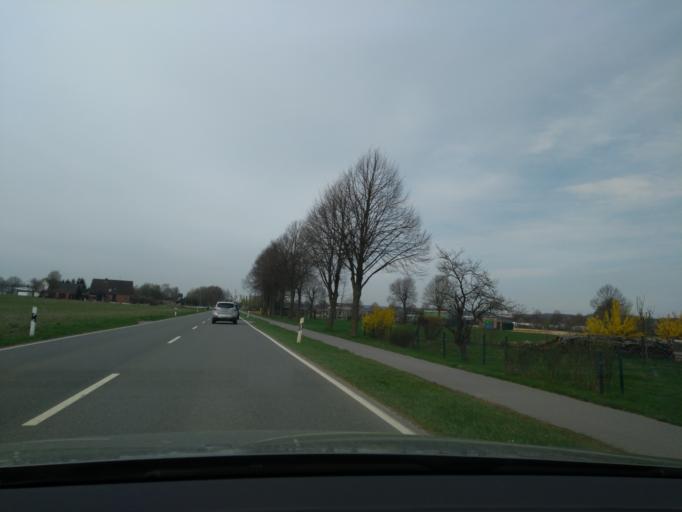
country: DE
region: North Rhine-Westphalia
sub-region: Regierungsbezirk Dusseldorf
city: Sonsbeck
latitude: 51.5972
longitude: 6.3944
